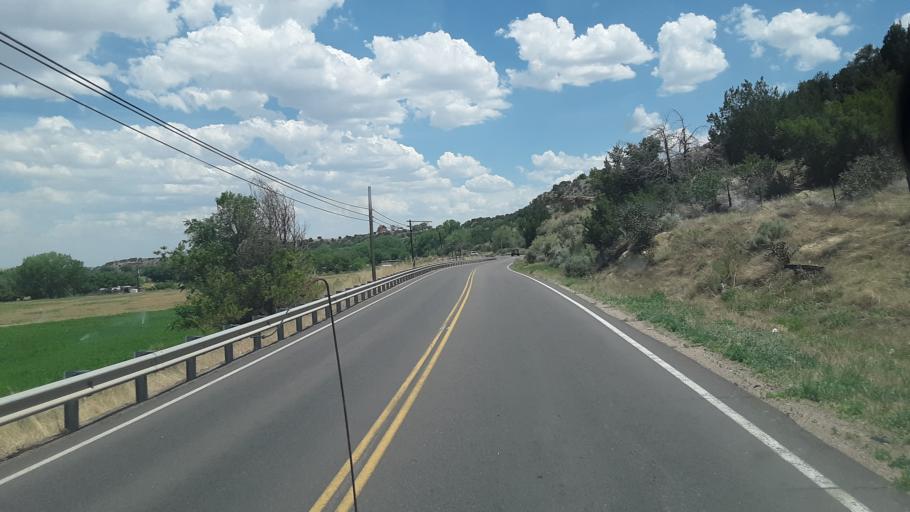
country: US
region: Colorado
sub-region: Fremont County
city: Lincoln Park
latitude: 38.4091
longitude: -105.1714
